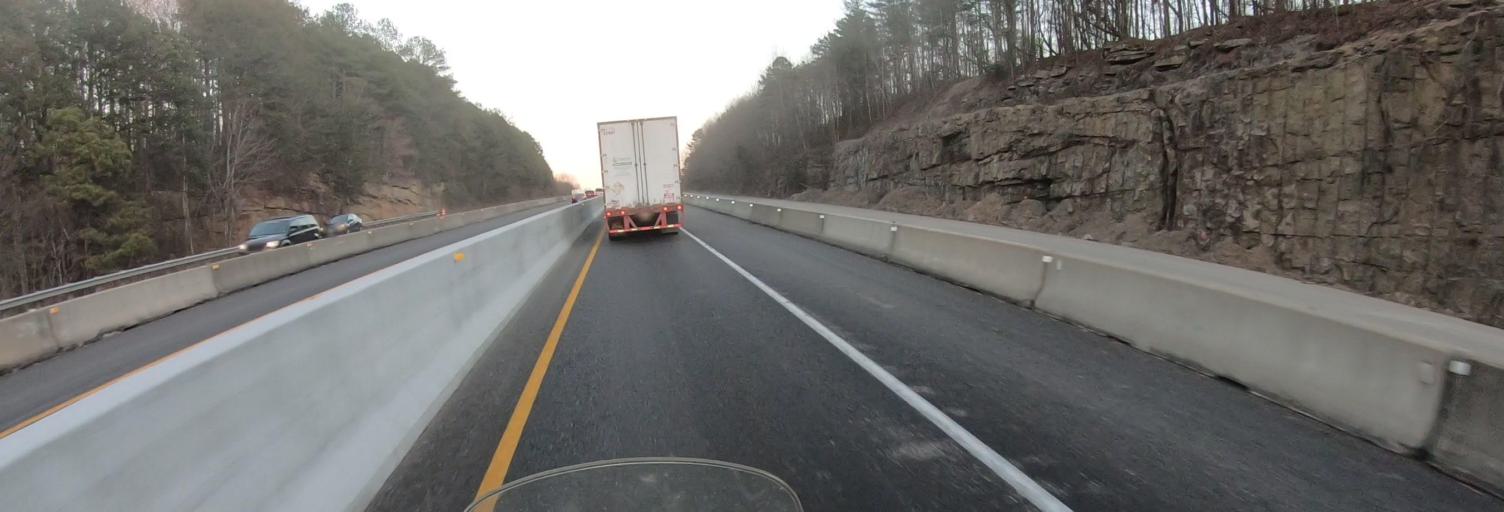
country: US
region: Kentucky
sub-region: Laurel County
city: London
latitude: 37.2101
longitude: -84.1820
